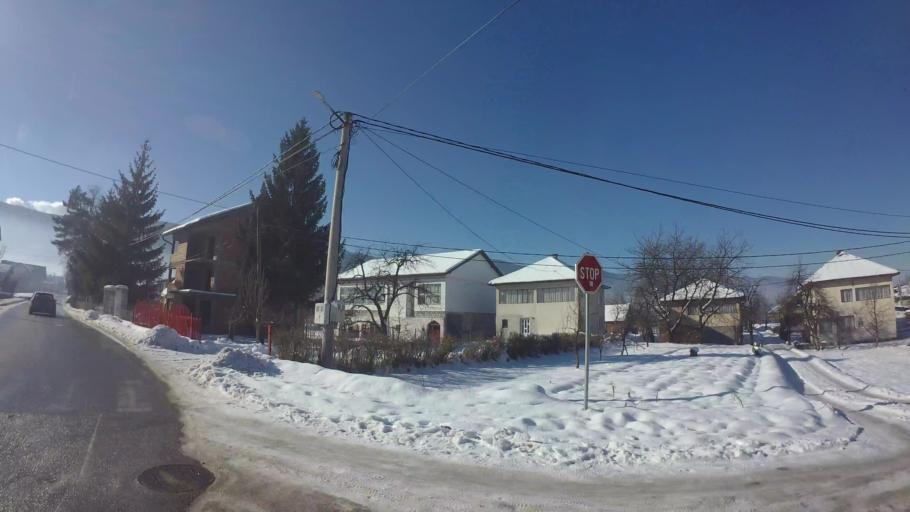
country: BA
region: Federation of Bosnia and Herzegovina
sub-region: Kanton Sarajevo
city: Sarajevo
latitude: 43.7975
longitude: 18.3479
